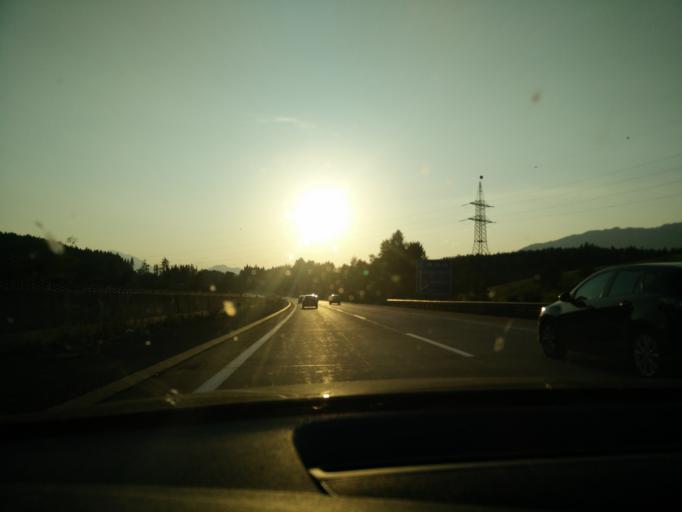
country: AT
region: Carinthia
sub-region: Politischer Bezirk Villach Land
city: Wernberg
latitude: 46.6237
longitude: 13.9694
